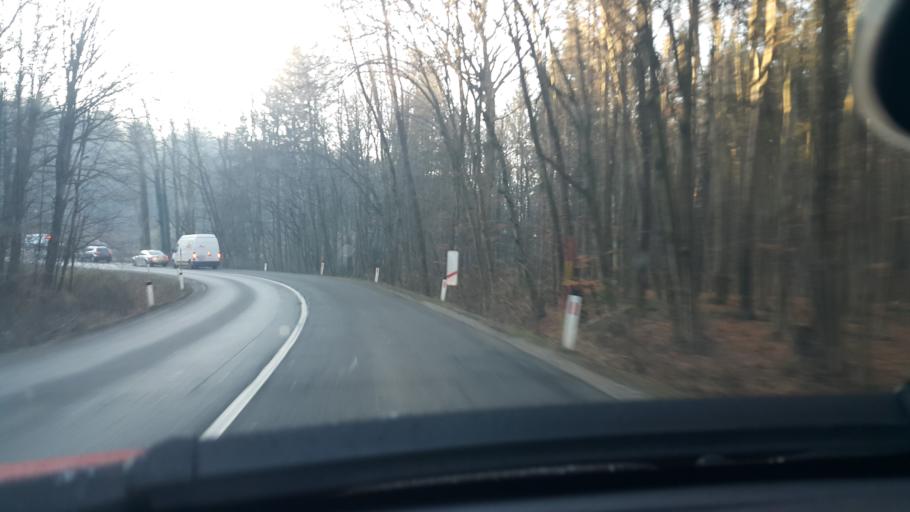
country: SI
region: Slovenska Bistrica
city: Slovenska Bistrica
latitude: 46.3582
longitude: 15.5701
